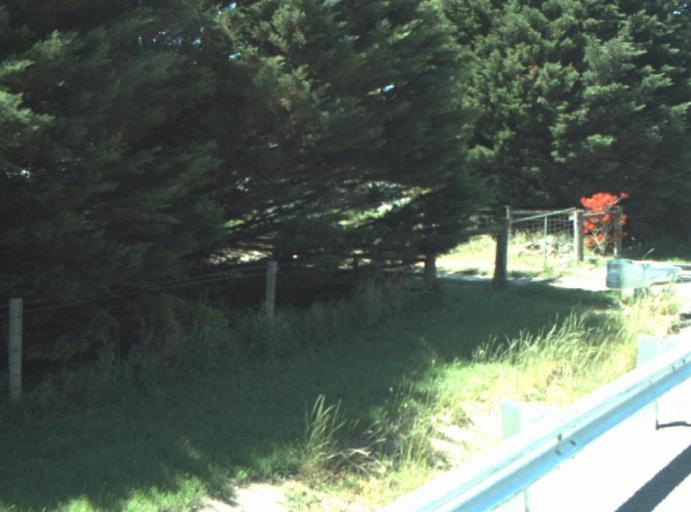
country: AU
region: Victoria
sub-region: Greater Geelong
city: Breakwater
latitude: -38.2060
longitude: 144.3611
